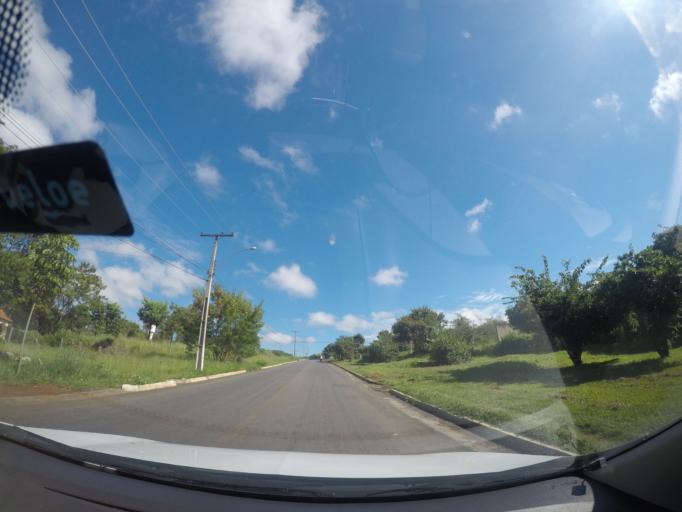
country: BR
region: Goias
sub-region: Senador Canedo
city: Senador Canedo
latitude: -16.6589
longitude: -49.1530
